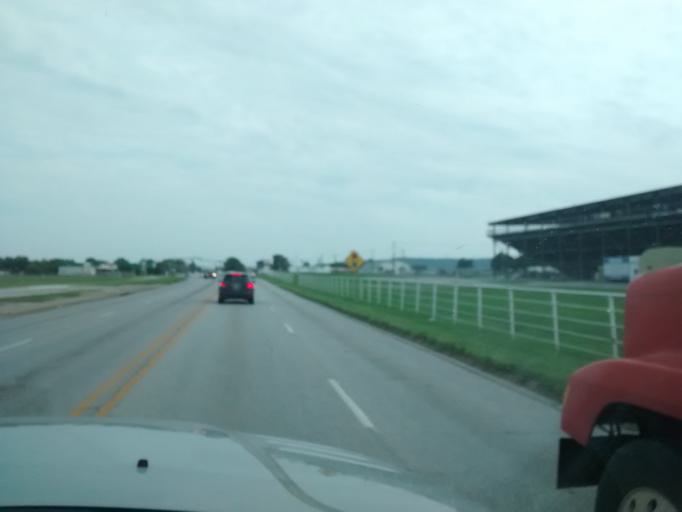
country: US
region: Arkansas
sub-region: Washington County
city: Springdale
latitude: 36.1821
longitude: -94.1164
